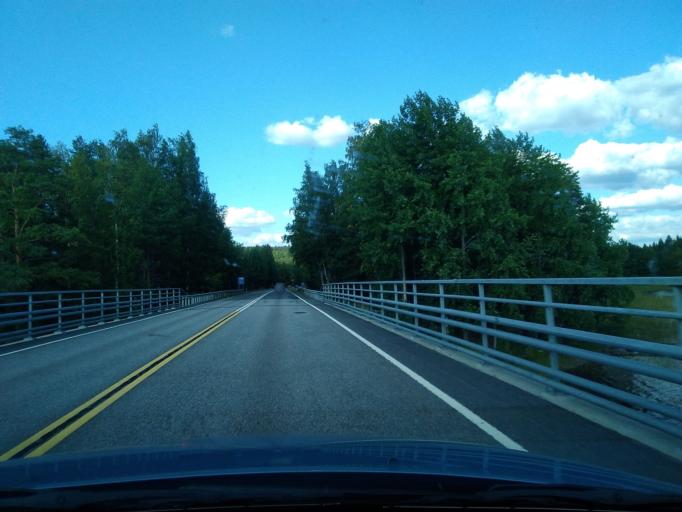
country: FI
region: Pirkanmaa
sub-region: Ylae-Pirkanmaa
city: Maenttae
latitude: 61.9983
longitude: 24.6395
